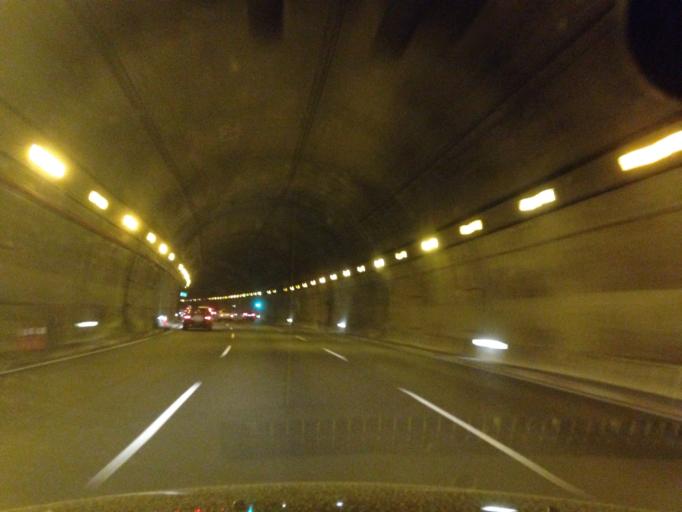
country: ES
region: Andalusia
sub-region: Provincia de Malaga
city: Malaga
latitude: 36.7379
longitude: -4.3783
